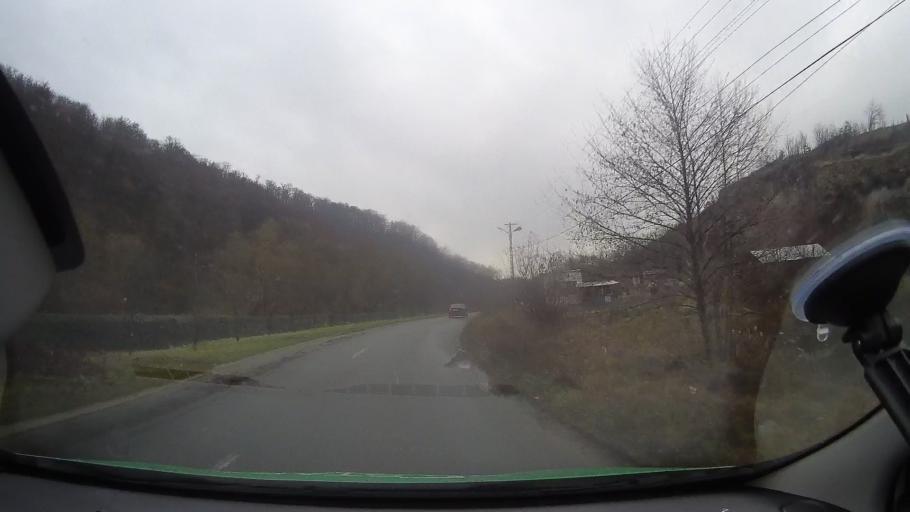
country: RO
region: Arad
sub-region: Comuna Sebis
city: Sebis
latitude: 46.3802
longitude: 22.1405
